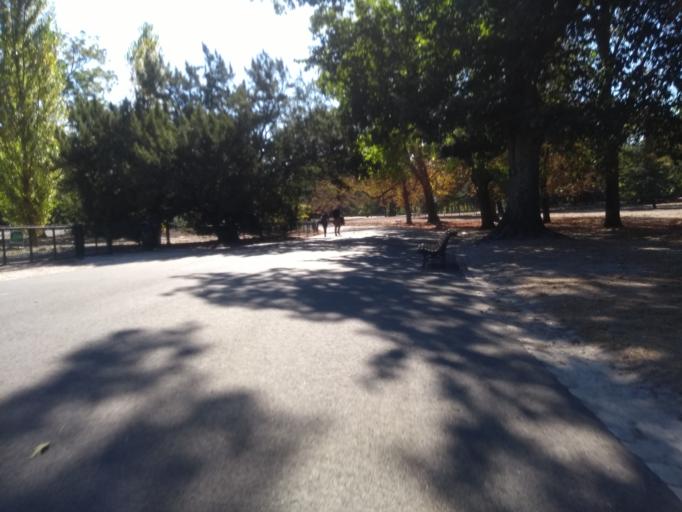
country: FR
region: Aquitaine
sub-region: Departement de la Gironde
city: Le Bouscat
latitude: 44.8523
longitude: -0.6022
